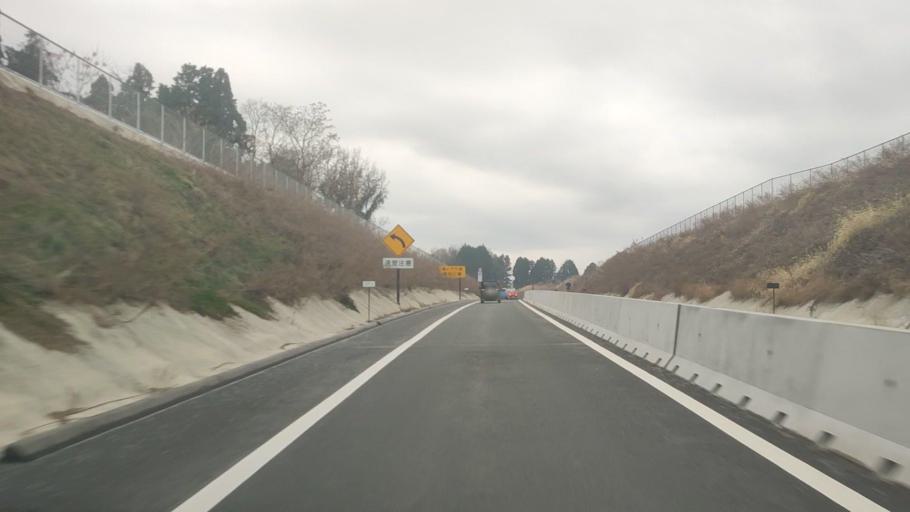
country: JP
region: Kumamoto
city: Ozu
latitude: 32.8972
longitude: 130.8989
